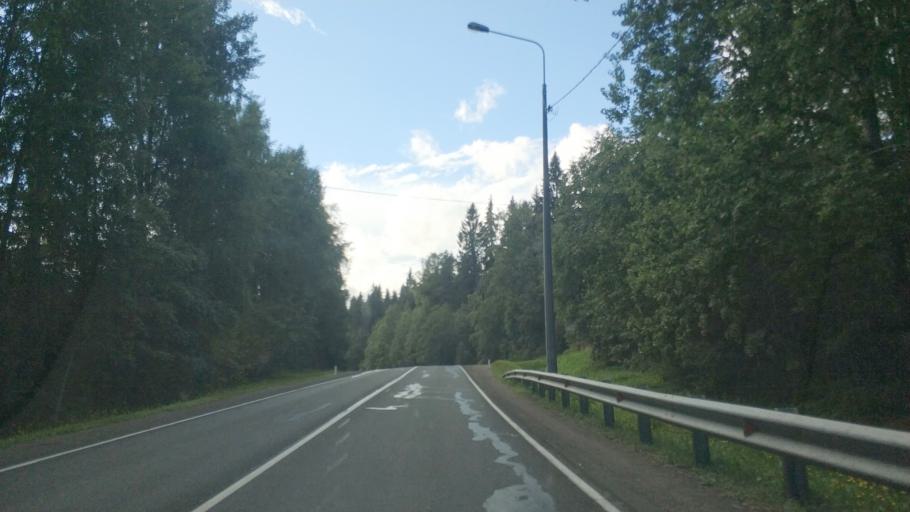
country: RU
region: Republic of Karelia
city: Lakhdenpokh'ya
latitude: 61.5115
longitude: 30.0794
